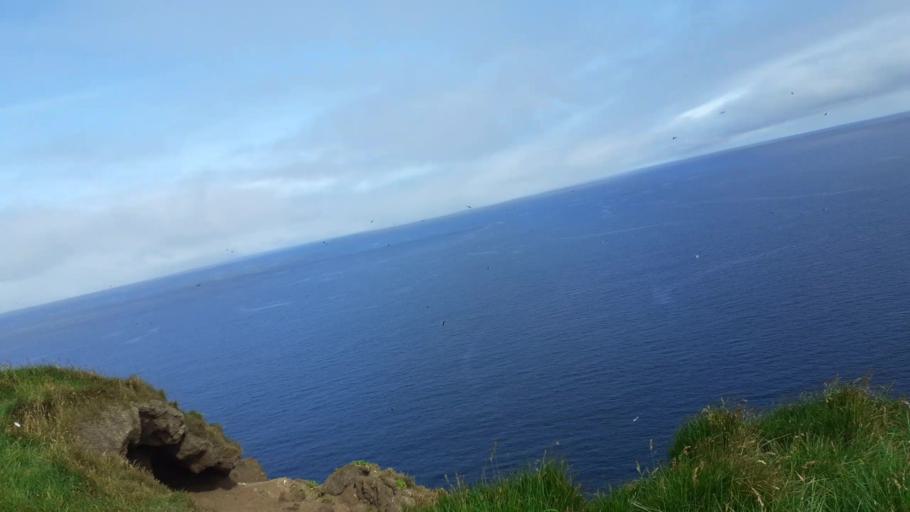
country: IS
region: Northeast
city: Dalvik
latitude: 66.5532
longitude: -17.9987
